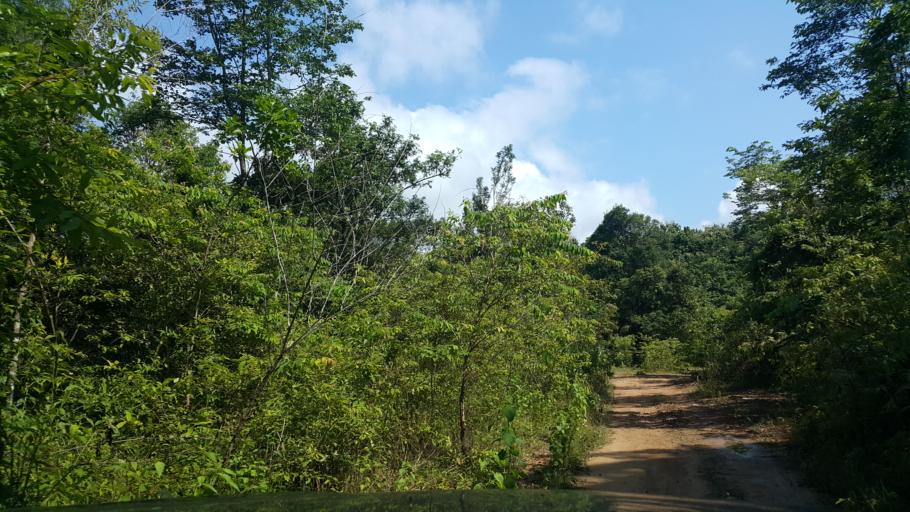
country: TH
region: Chiang Mai
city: San Sai
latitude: 18.9543
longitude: 99.1379
